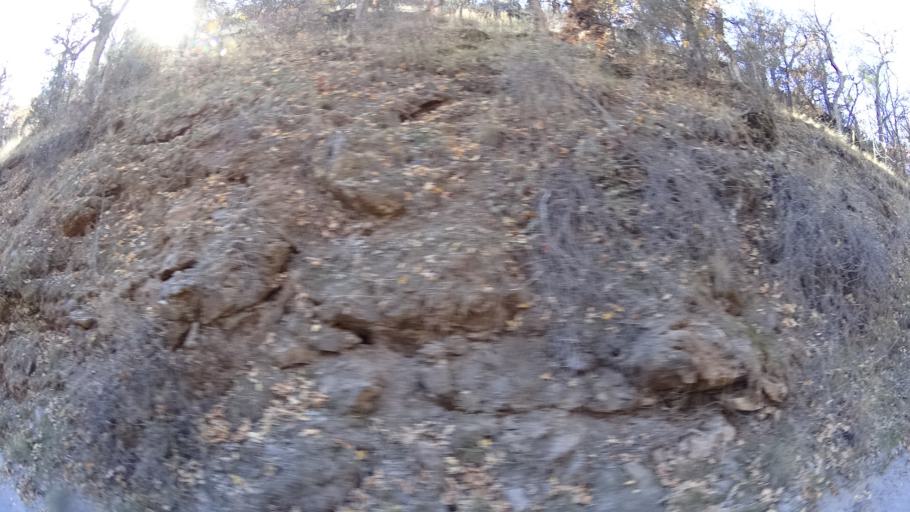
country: US
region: California
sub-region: Siskiyou County
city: Yreka
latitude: 41.8294
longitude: -122.6518
